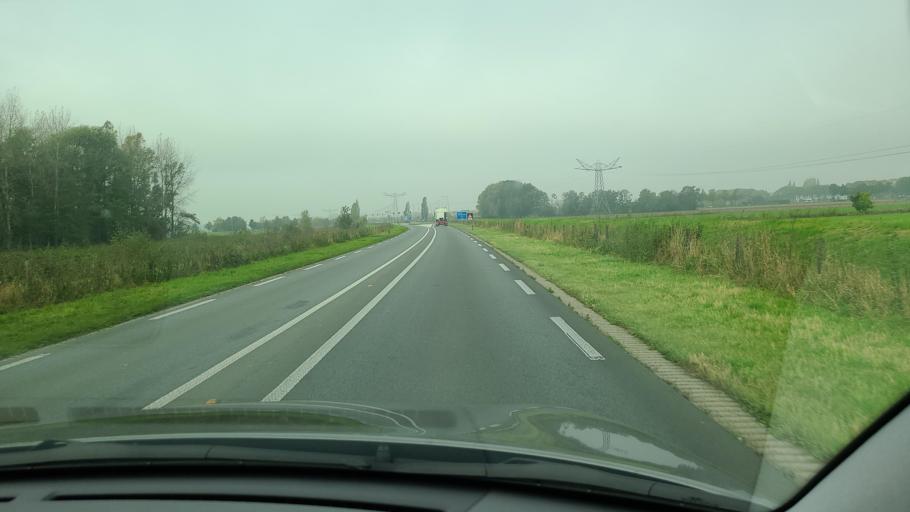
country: NL
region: Gelderland
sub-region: Gemeente Druten
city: Druten
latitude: 51.8723
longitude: 5.5389
